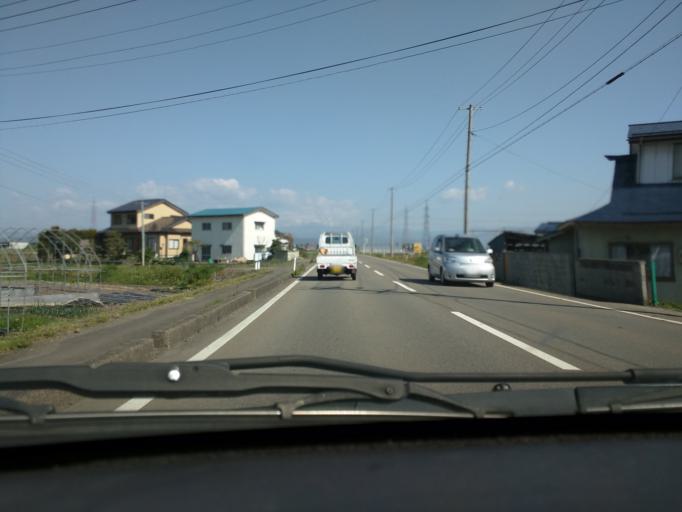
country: JP
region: Fukushima
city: Kitakata
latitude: 37.5719
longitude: 139.8997
